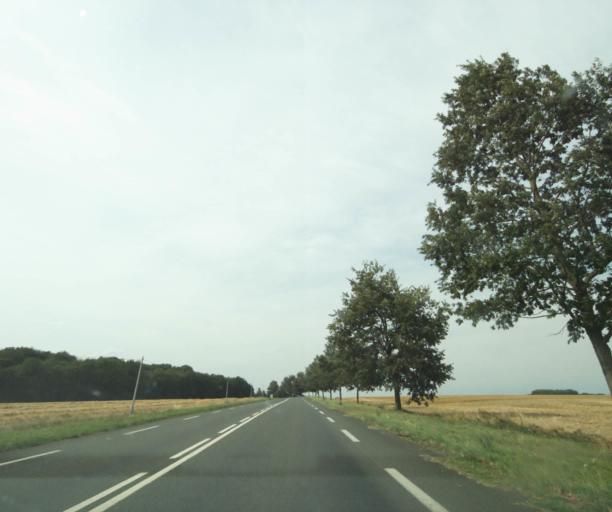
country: FR
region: Centre
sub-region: Departement d'Indre-et-Loire
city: Saint-Christophe-sur-le-Nais
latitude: 47.6447
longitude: 0.4974
